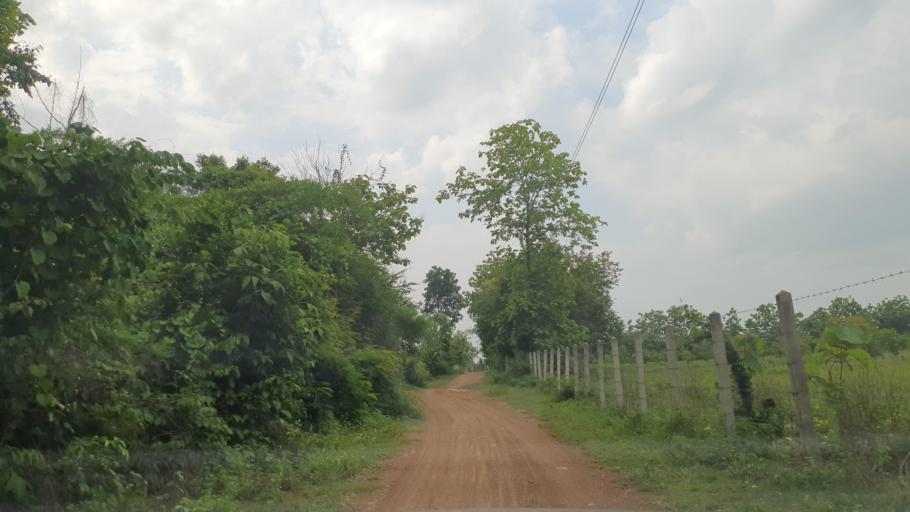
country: TH
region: Sukhothai
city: Thung Saliam
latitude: 17.2447
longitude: 99.5439
